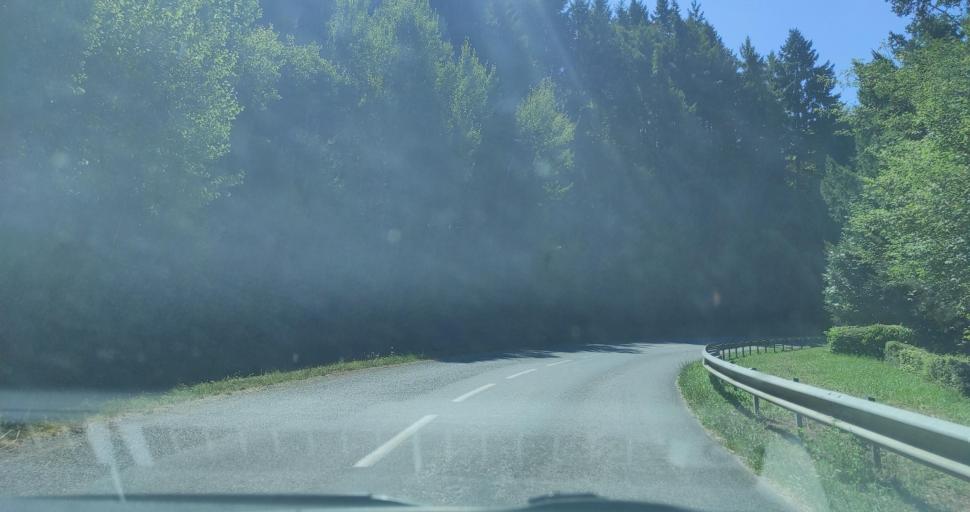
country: FR
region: Midi-Pyrenees
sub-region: Departement de l'Aveyron
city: Firmi
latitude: 44.5192
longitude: 2.3093
